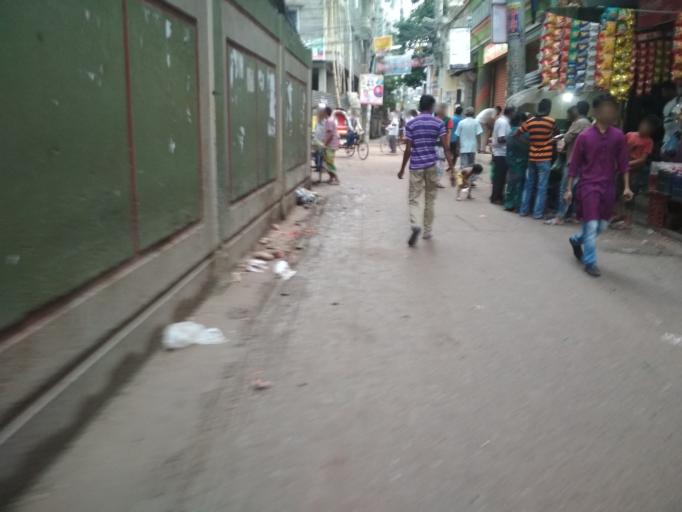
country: BD
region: Dhaka
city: Azimpur
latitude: 23.8040
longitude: 90.3663
